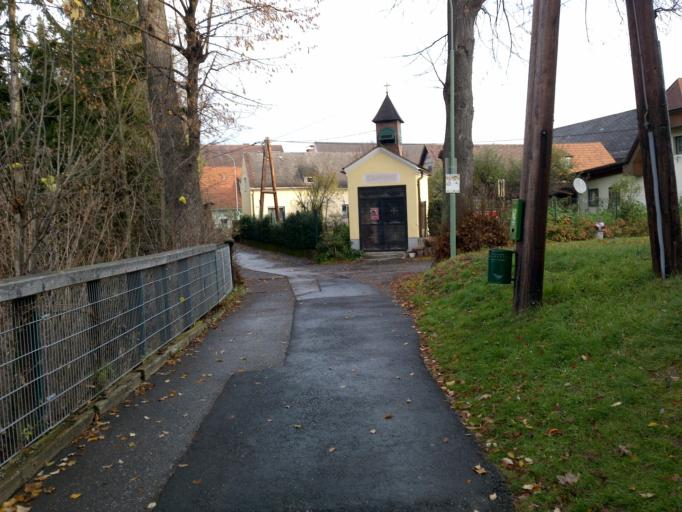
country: AT
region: Styria
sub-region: Politischer Bezirk Murtal
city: Judenburg
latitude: 47.1718
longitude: 14.6775
